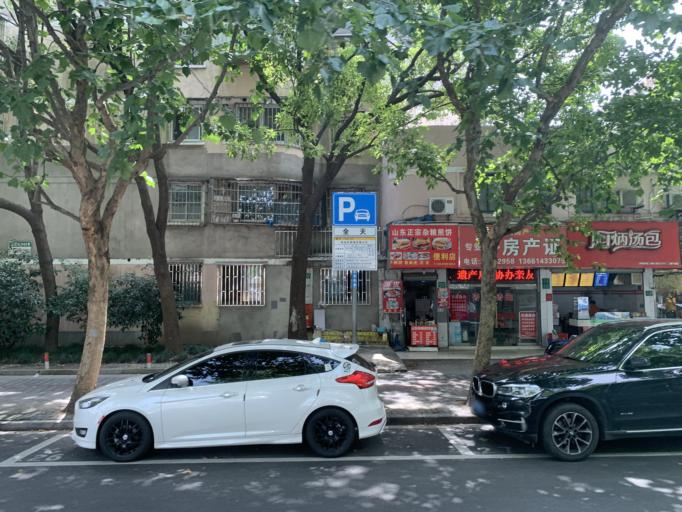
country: CN
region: Shanghai Shi
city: Pudong
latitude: 31.2490
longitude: 121.5598
